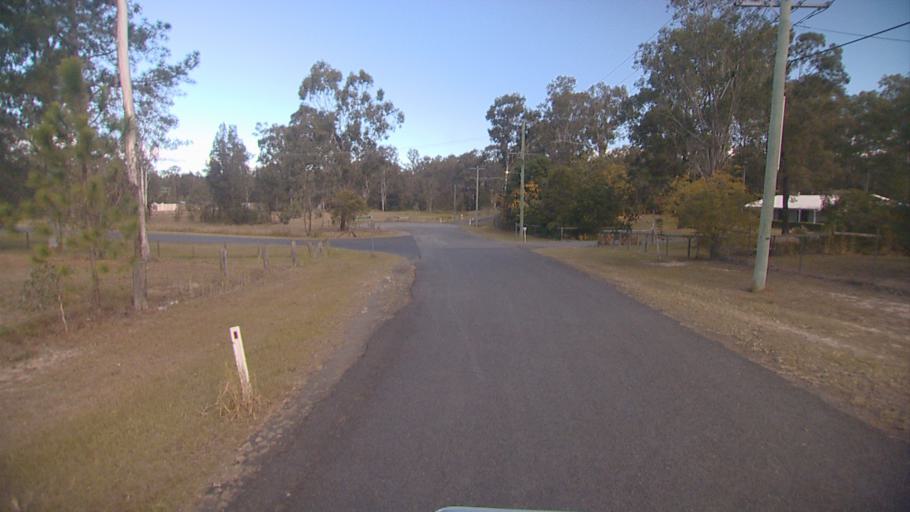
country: AU
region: Queensland
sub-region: Logan
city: North Maclean
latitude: -27.8191
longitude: 153.0458
